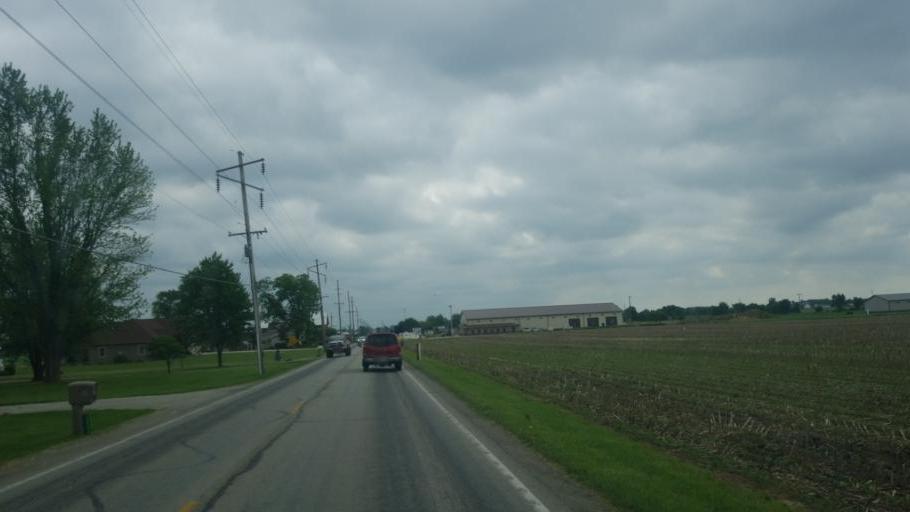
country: US
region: Indiana
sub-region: Elkhart County
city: Nappanee
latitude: 41.4287
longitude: -86.0013
